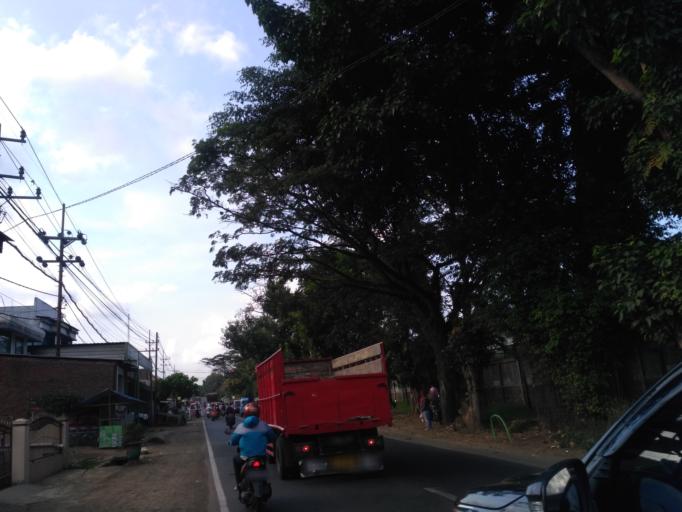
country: ID
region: East Java
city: Wadung
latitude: -8.0486
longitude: 112.6068
